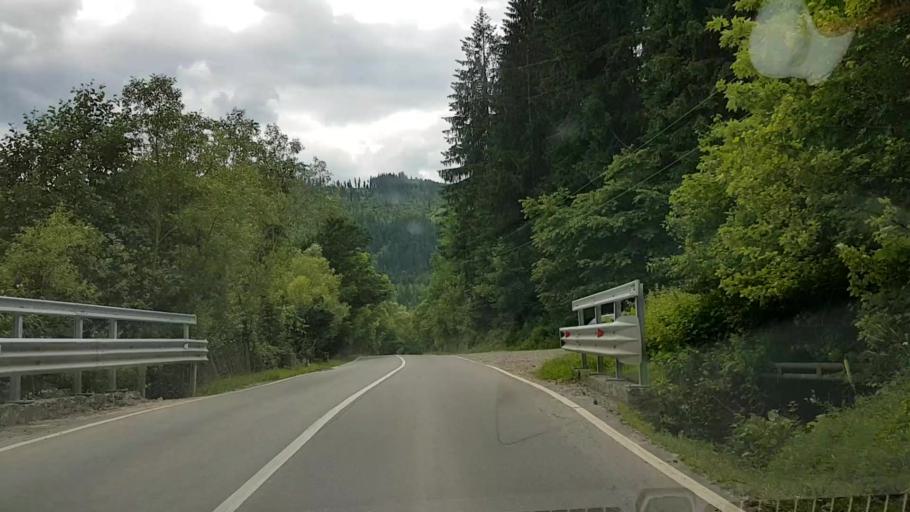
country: RO
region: Neamt
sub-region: Comuna Poiana Teiului
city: Poiana Teiului
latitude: 47.1004
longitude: 25.9413
